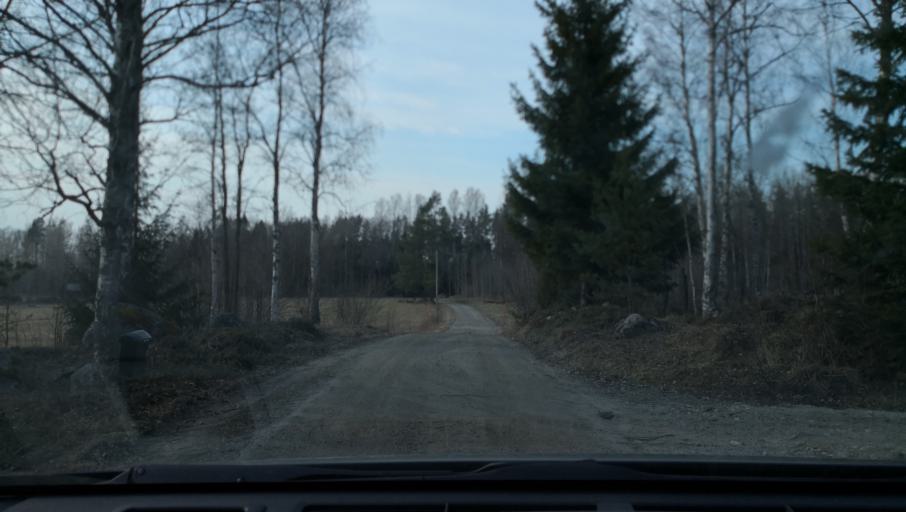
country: SE
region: OErebro
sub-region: Lindesbergs Kommun
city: Frovi
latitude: 59.3861
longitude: 15.3625
